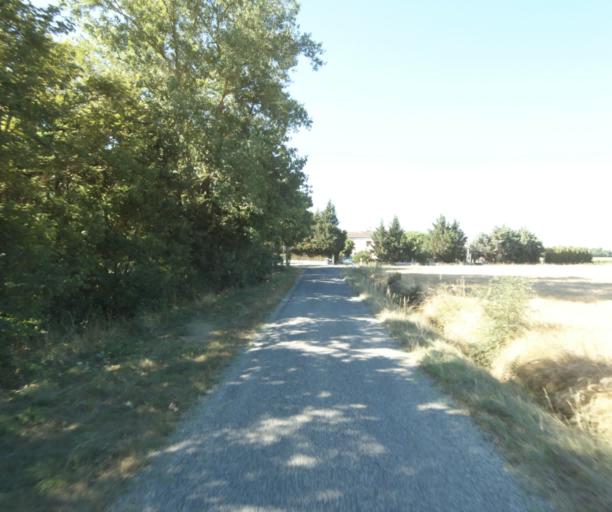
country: FR
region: Midi-Pyrenees
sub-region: Departement de la Haute-Garonne
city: Revel
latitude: 43.4860
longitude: 1.9527
